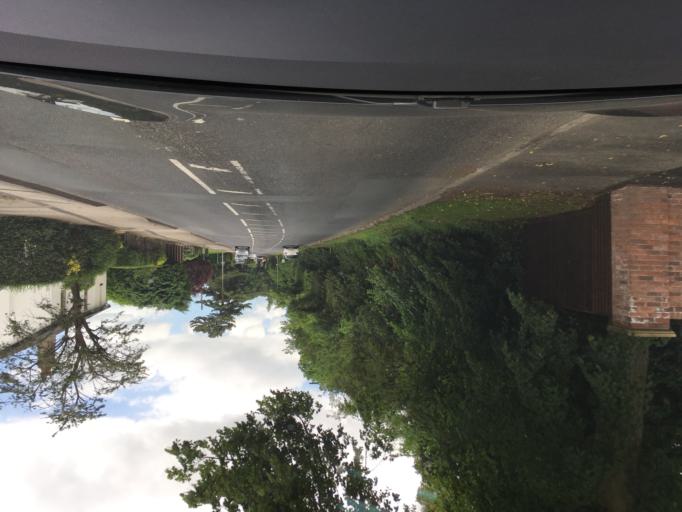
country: GB
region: England
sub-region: Cheshire East
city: Knutsford
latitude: 53.2968
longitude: -2.3601
